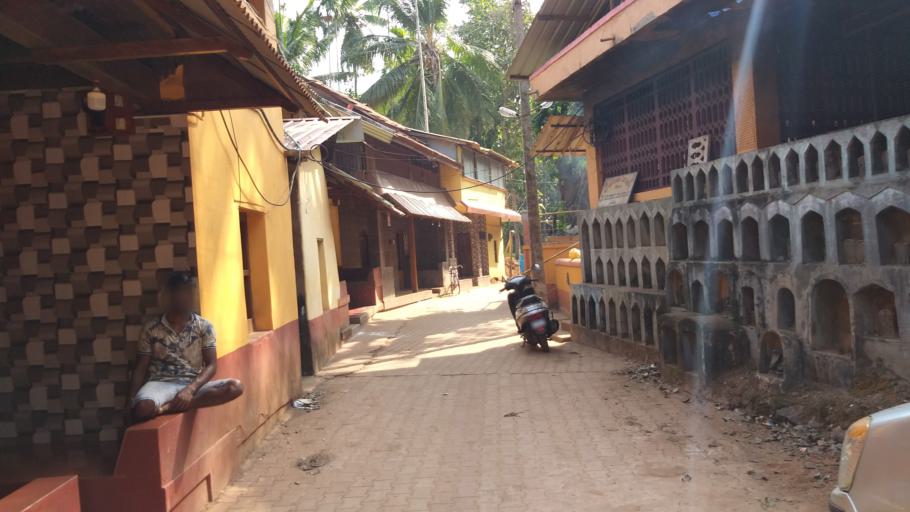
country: IN
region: Karnataka
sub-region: Uttar Kannada
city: Gokarna
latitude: 14.5426
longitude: 74.3174
